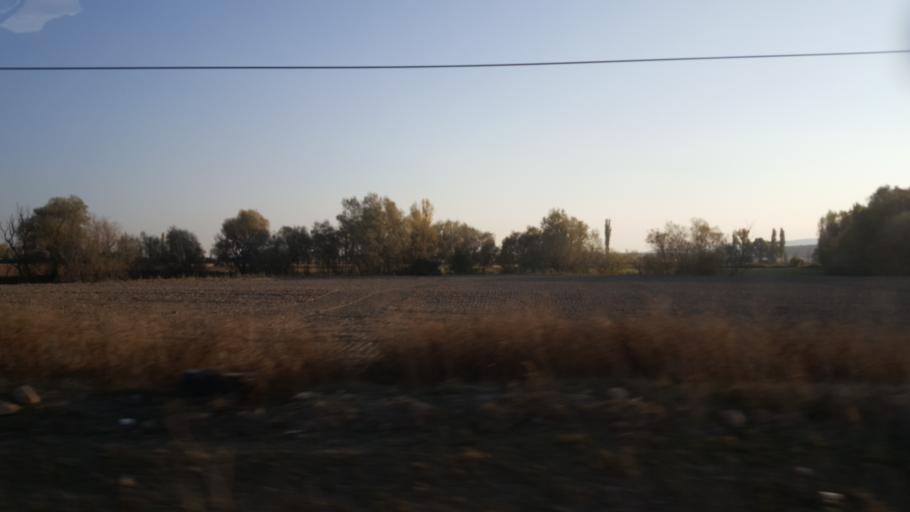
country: TR
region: Eskisehir
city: Mahmudiye
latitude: 39.5758
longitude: 30.9052
